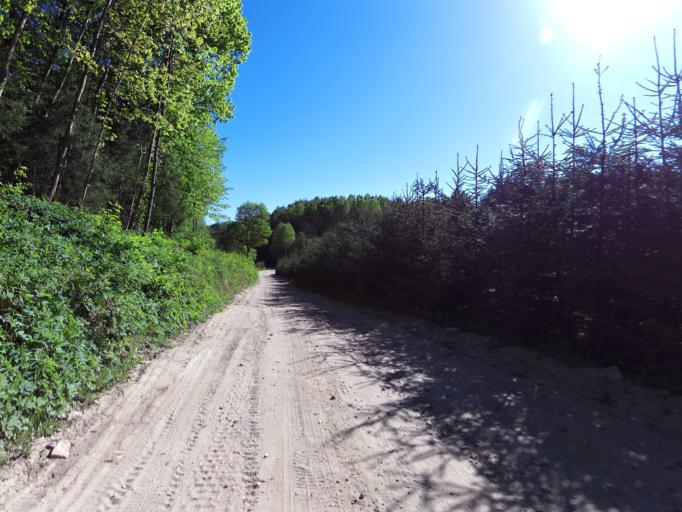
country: LT
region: Vilnius County
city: Pilaite
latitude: 54.6919
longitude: 25.1551
